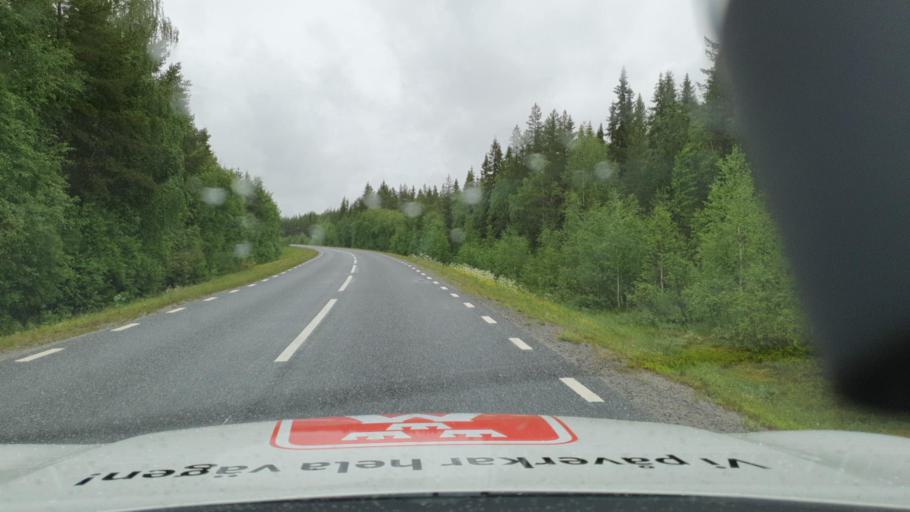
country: SE
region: Vaesterbotten
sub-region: Asele Kommun
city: Asele
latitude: 63.9820
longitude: 17.2649
